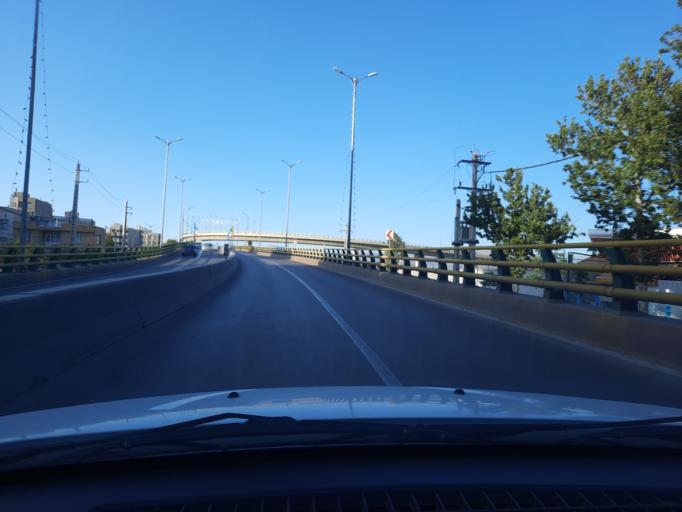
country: IR
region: Qazvin
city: Qazvin
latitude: 36.2721
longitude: 50.0230
